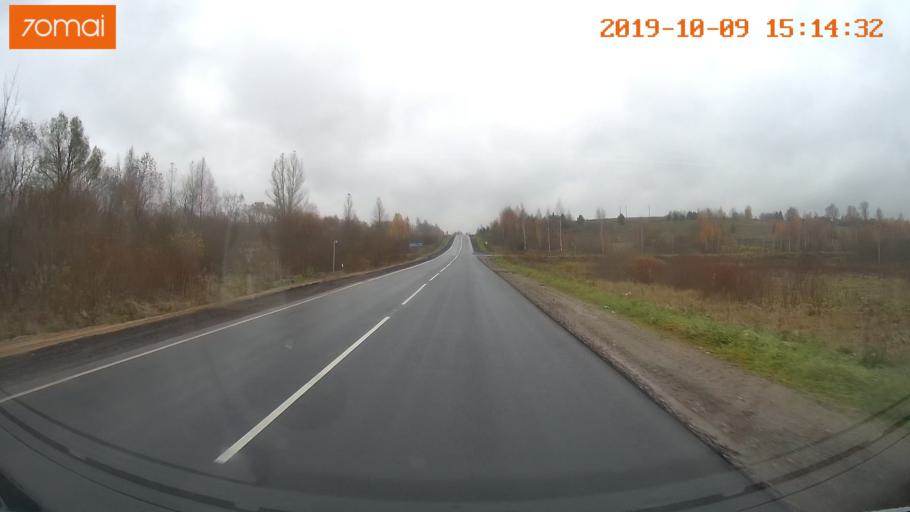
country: RU
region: Kostroma
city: Susanino
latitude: 58.1335
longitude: 41.6022
